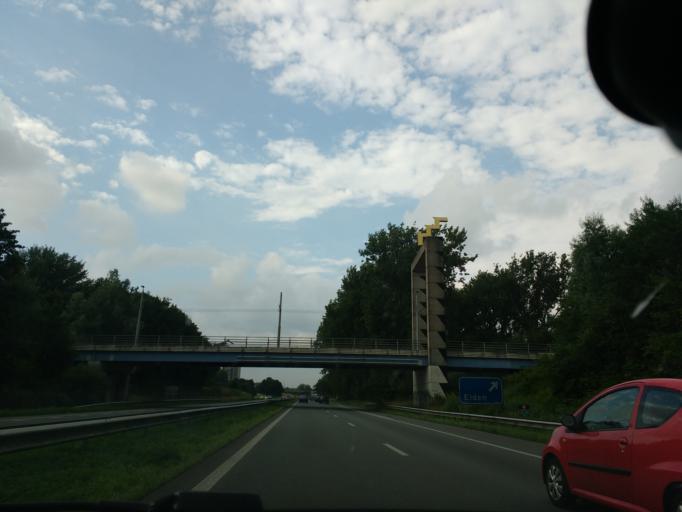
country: NL
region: Gelderland
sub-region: Gemeente Overbetuwe
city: Elst
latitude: 51.9455
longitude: 5.8788
